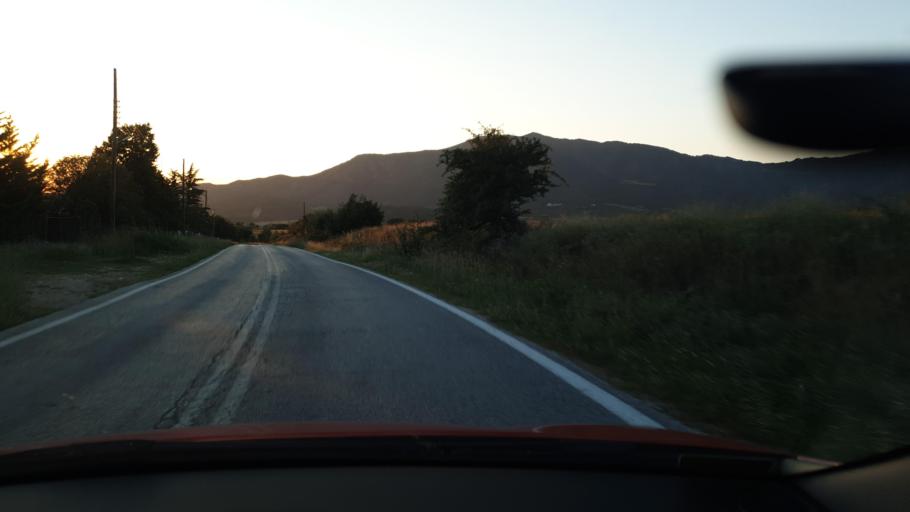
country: GR
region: Central Macedonia
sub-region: Nomos Chalkidikis
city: Galatista
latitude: 40.4694
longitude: 23.2573
